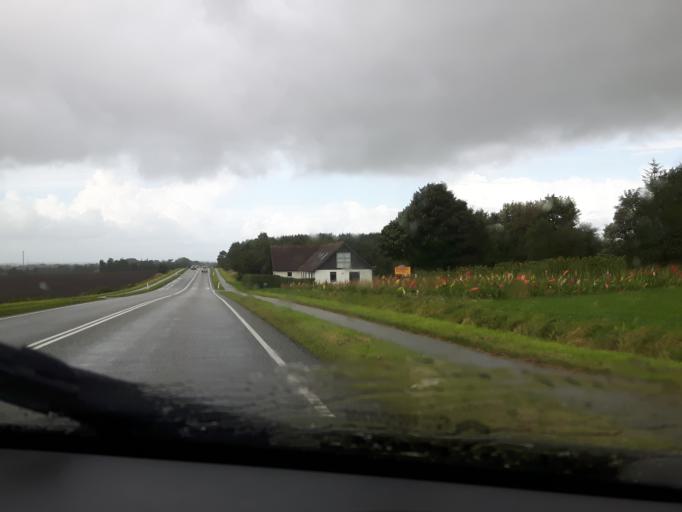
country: DK
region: North Denmark
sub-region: Jammerbugt Kommune
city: Fjerritslev
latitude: 57.0878
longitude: 9.3018
